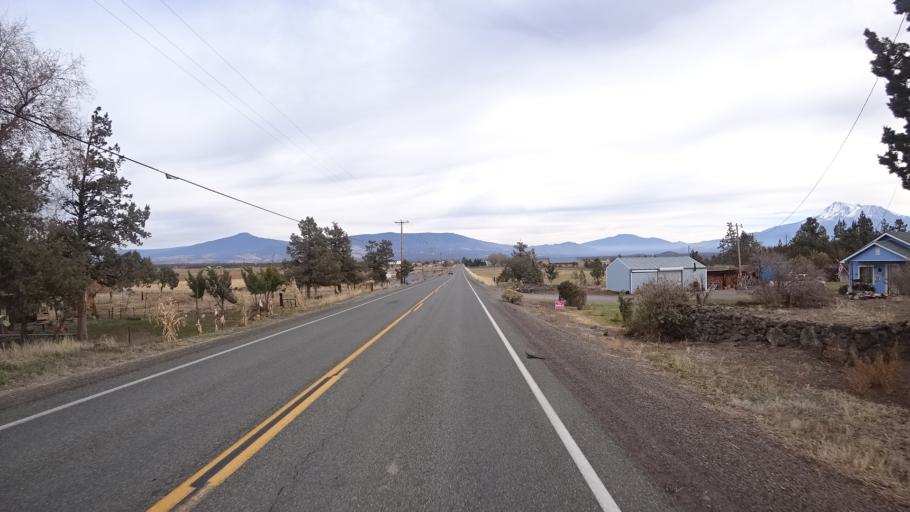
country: US
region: California
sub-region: Siskiyou County
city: Montague
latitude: 41.6240
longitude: -122.4188
